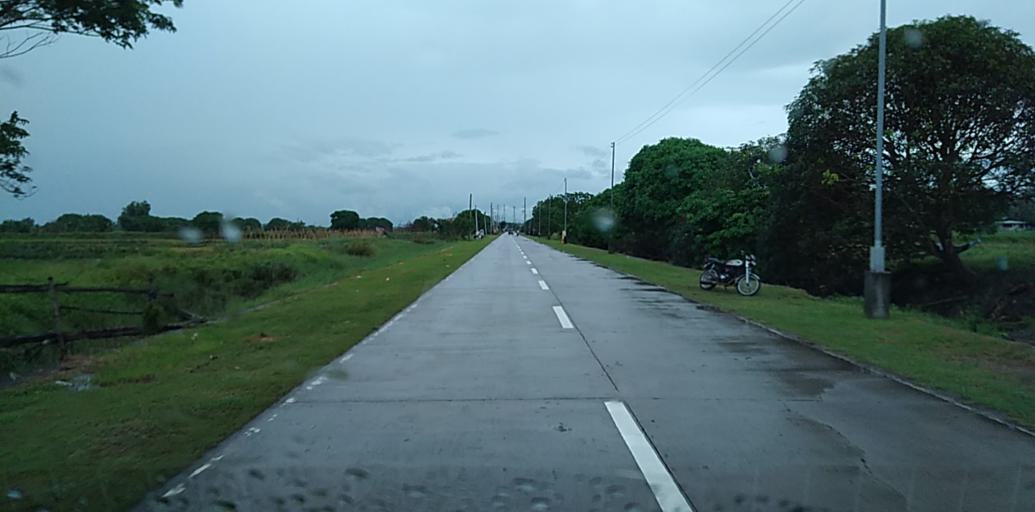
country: PH
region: Central Luzon
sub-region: Province of Pampanga
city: Salapungan
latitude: 15.1329
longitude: 120.8950
